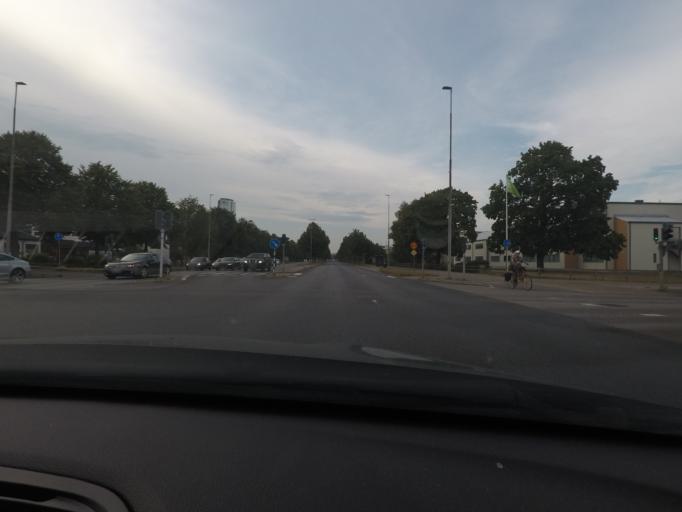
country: SE
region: Halland
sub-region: Halmstads Kommun
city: Halmstad
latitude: 56.6631
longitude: 12.8851
